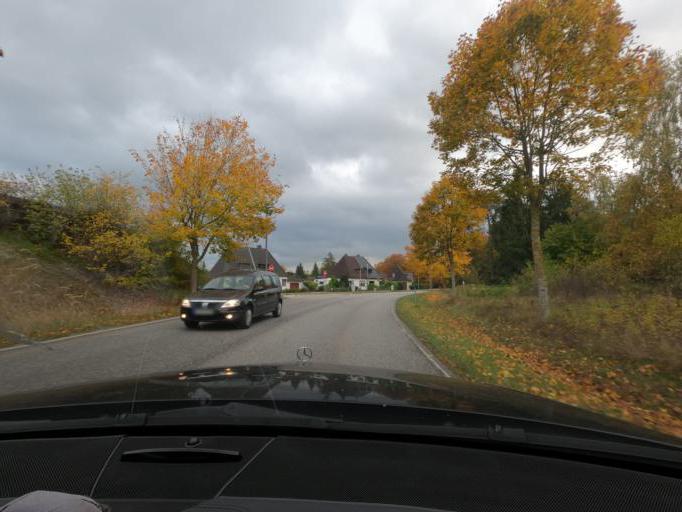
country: DE
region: Schleswig-Holstein
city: Geesthacht
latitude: 53.4506
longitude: 10.3685
